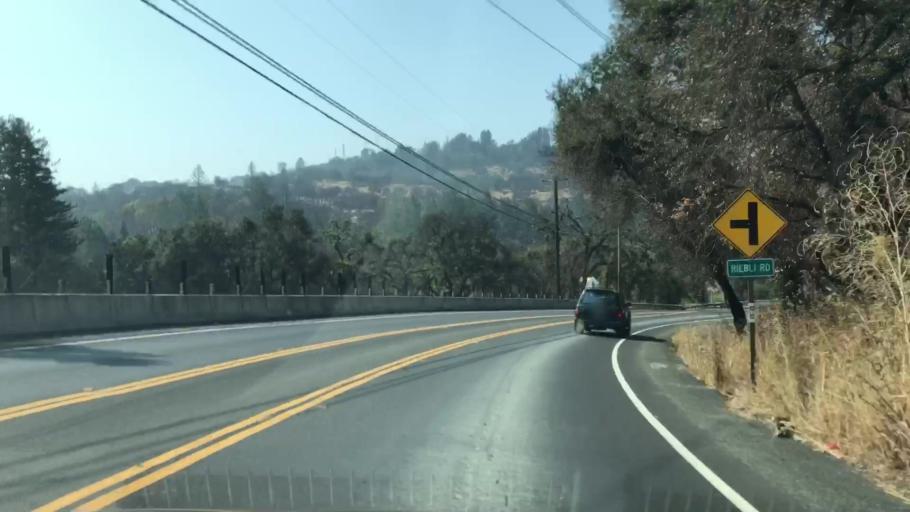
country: US
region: California
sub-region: Sonoma County
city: Larkfield-Wikiup
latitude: 38.5092
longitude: -122.7185
